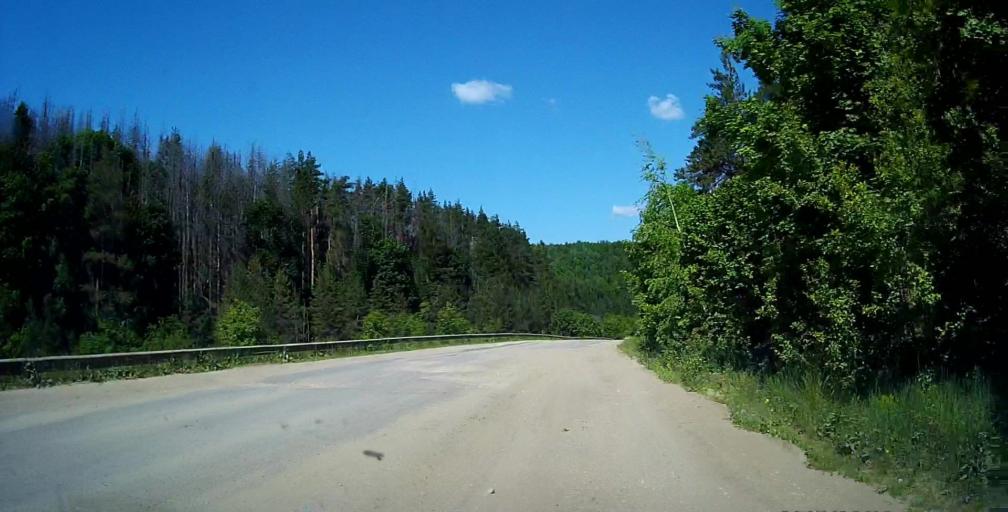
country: RU
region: Tula
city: Kurkino
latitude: 53.1991
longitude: 38.5714
